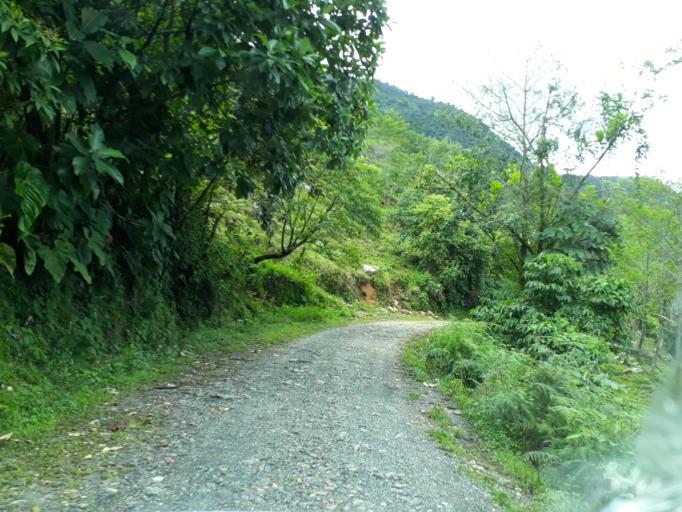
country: CO
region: Cundinamarca
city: Gachala
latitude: 4.7157
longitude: -73.3620
